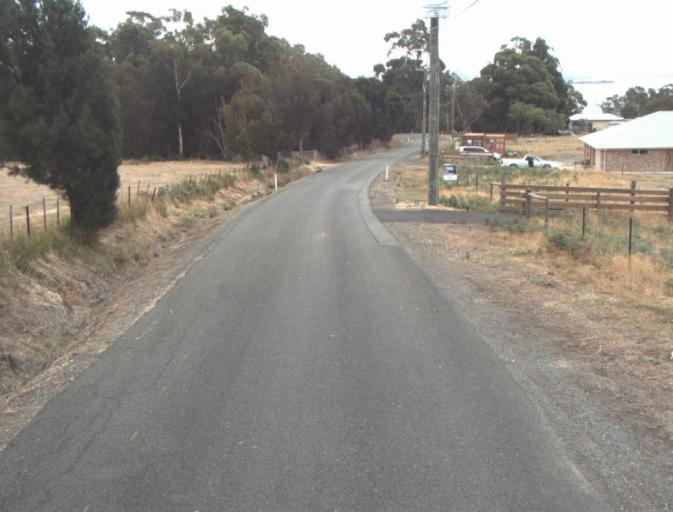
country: AU
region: Tasmania
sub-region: Launceston
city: Mayfield
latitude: -41.2834
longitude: 147.0225
